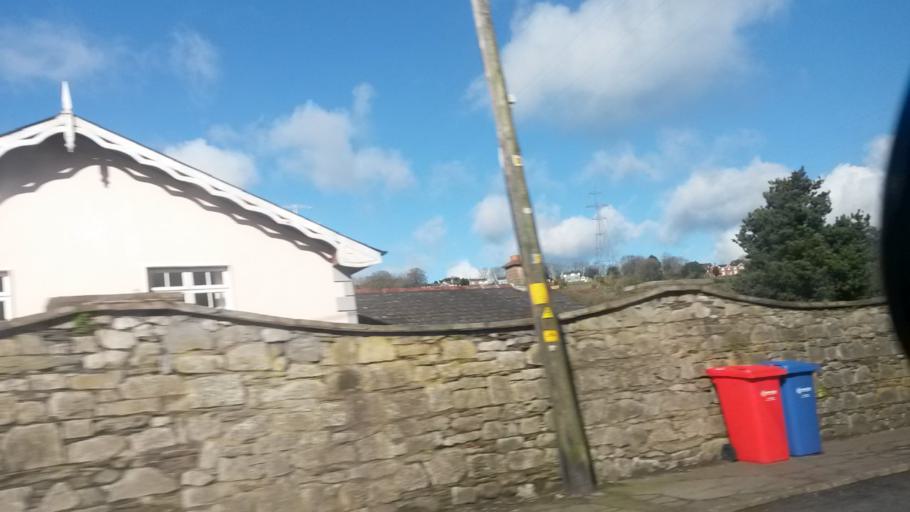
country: IE
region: Munster
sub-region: County Cork
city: Cobh
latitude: 51.8522
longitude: -8.3267
